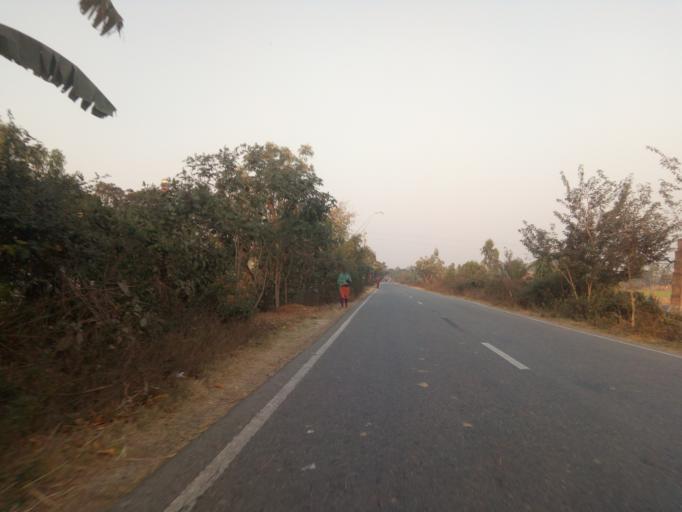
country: BD
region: Rajshahi
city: Bogra
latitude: 24.5879
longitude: 89.2320
